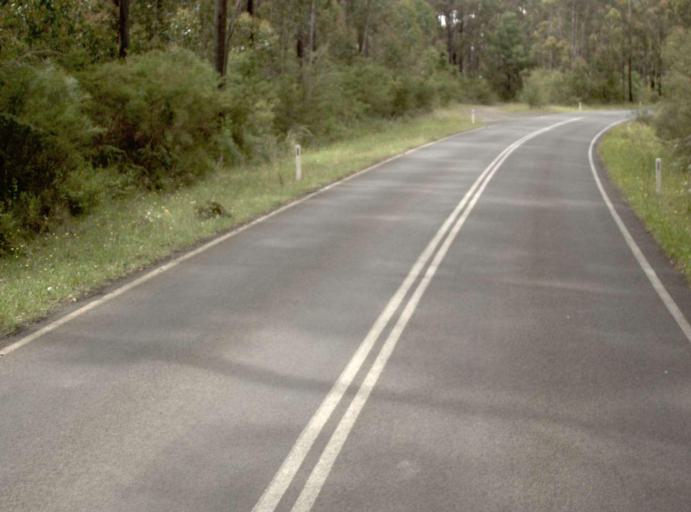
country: AU
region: Victoria
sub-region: Latrobe
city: Traralgon
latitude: -38.0292
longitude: 146.4205
